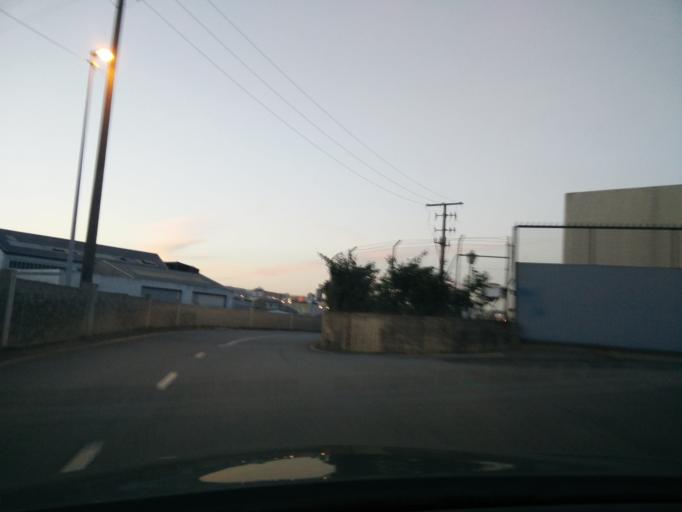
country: ES
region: Galicia
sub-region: Provincia da Coruna
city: A Coruna
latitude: 43.3456
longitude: -8.4255
